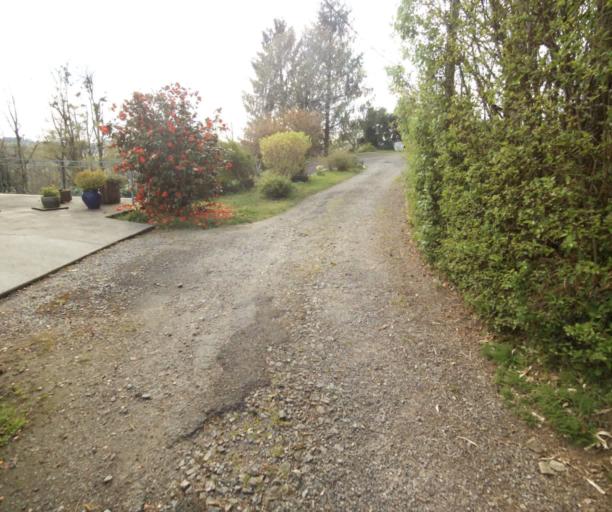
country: FR
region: Limousin
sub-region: Departement de la Correze
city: Tulle
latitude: 45.2506
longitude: 1.7451
